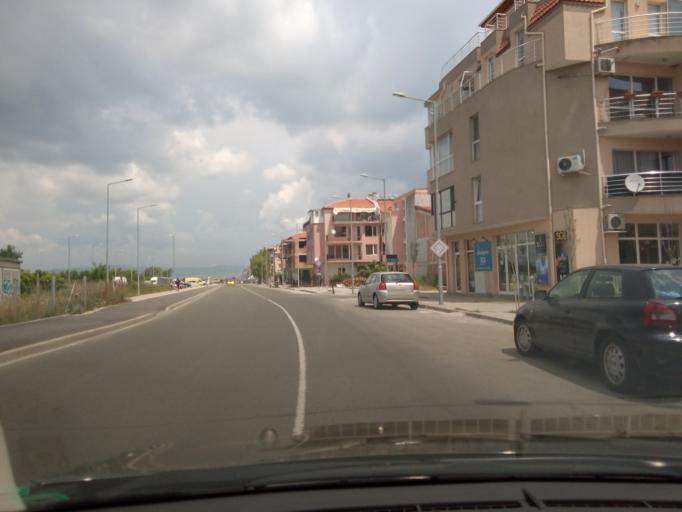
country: BG
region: Burgas
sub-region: Obshtina Nesebur
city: Ravda
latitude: 42.6539
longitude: 27.7025
